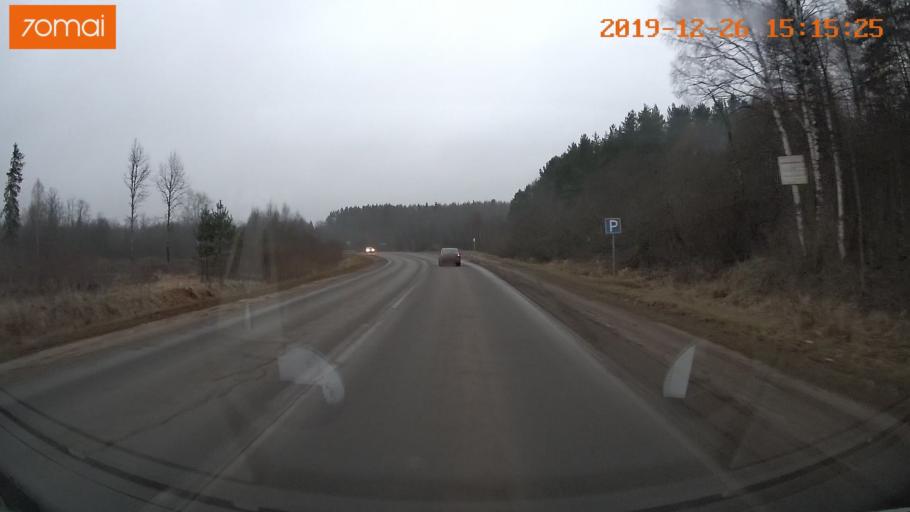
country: RU
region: Jaroslavl
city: Rybinsk
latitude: 58.0970
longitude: 38.8750
